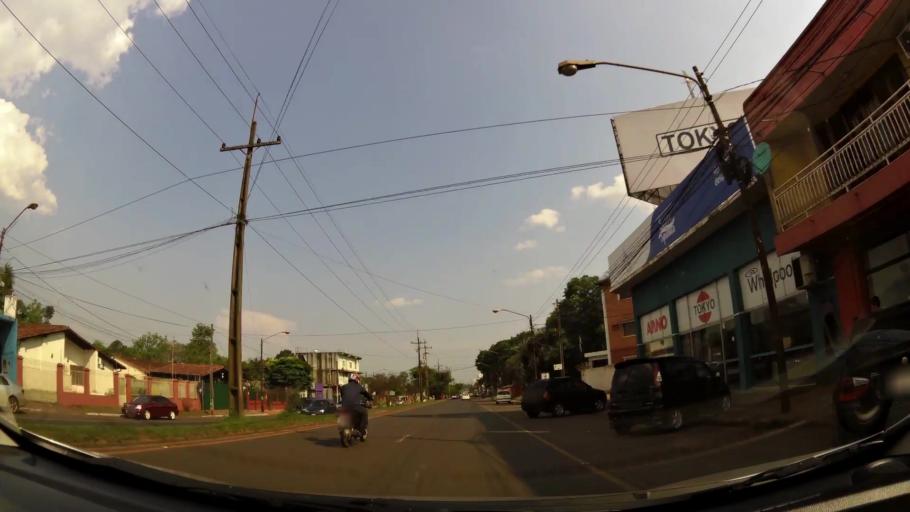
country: PY
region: Alto Parana
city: Presidente Franco
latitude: -25.5186
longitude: -54.6411
